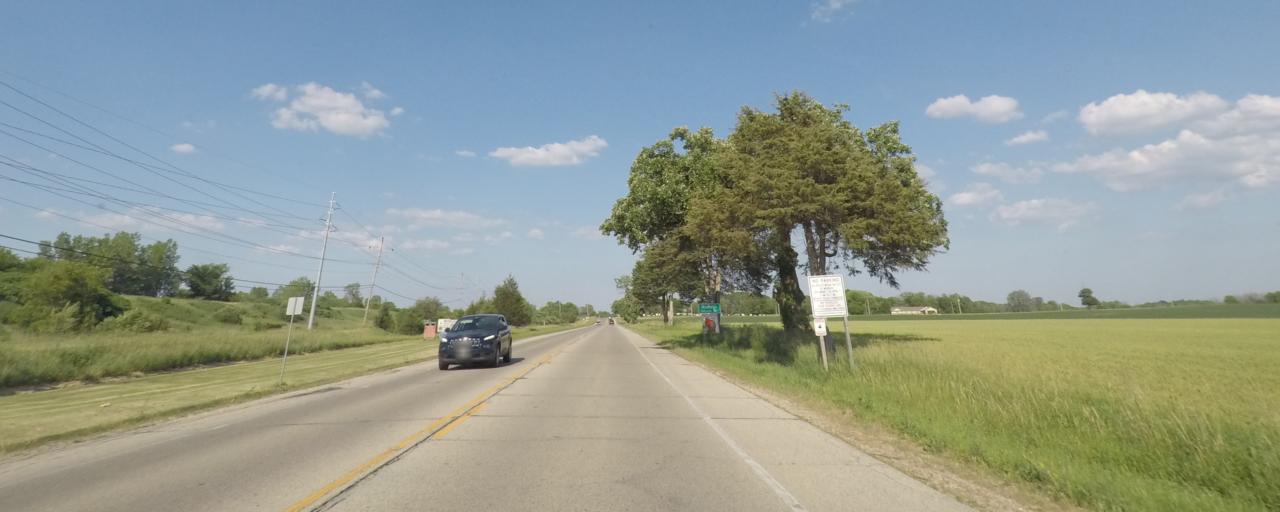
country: US
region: Wisconsin
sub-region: Waukesha County
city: Big Bend
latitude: 42.8871
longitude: -88.1915
